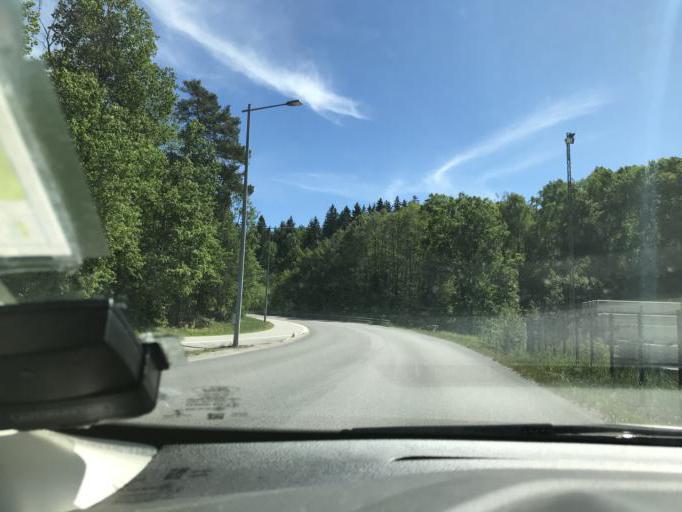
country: SE
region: Stockholm
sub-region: Botkyrka Kommun
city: Tumba
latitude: 59.2138
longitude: 17.8360
